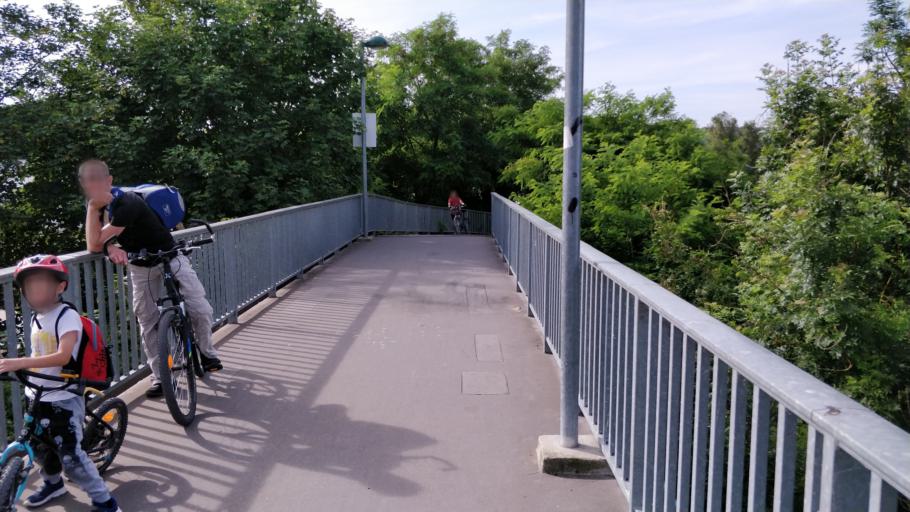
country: FR
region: Ile-de-France
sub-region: Departement de Seine-Saint-Denis
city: Noisy-le-Grand
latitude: 48.8646
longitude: 2.5660
